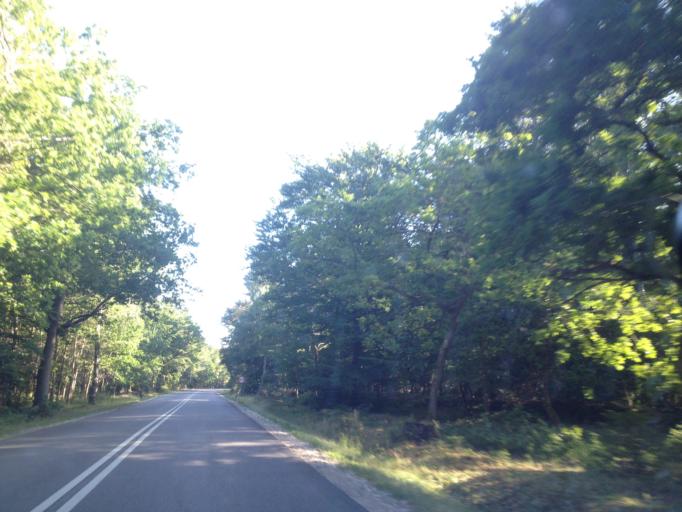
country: DK
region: Capital Region
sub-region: Halsnaes Kommune
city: Frederiksvaerk
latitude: 56.0255
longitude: 12.0810
